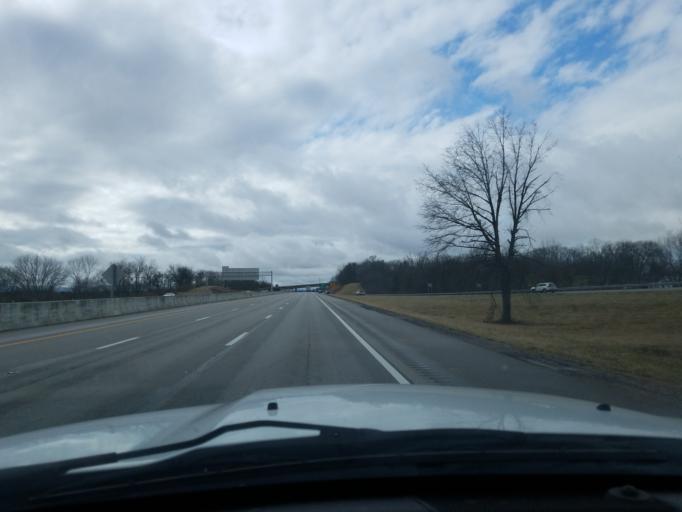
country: US
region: Kentucky
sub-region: Clark County
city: Winchester
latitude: 38.0190
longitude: -84.1509
